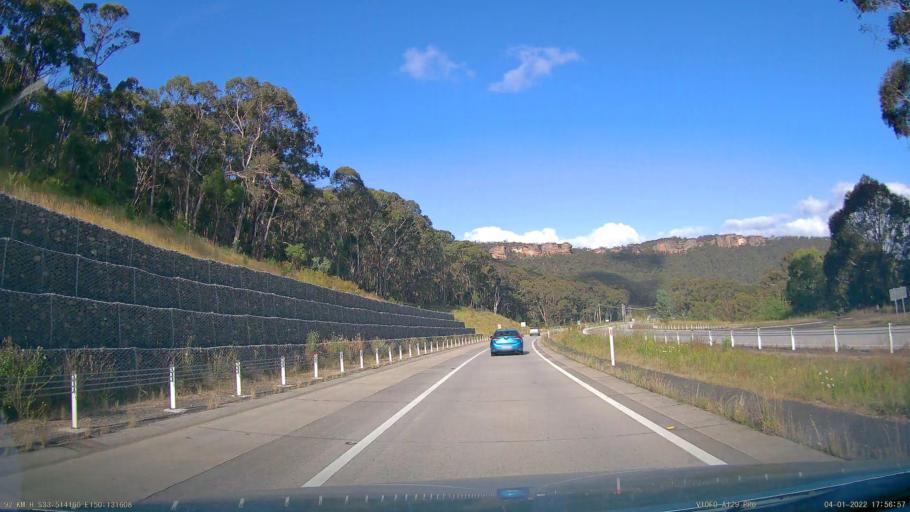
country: AU
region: New South Wales
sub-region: Lithgow
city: Bowenfels
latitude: -33.5142
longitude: 150.1319
